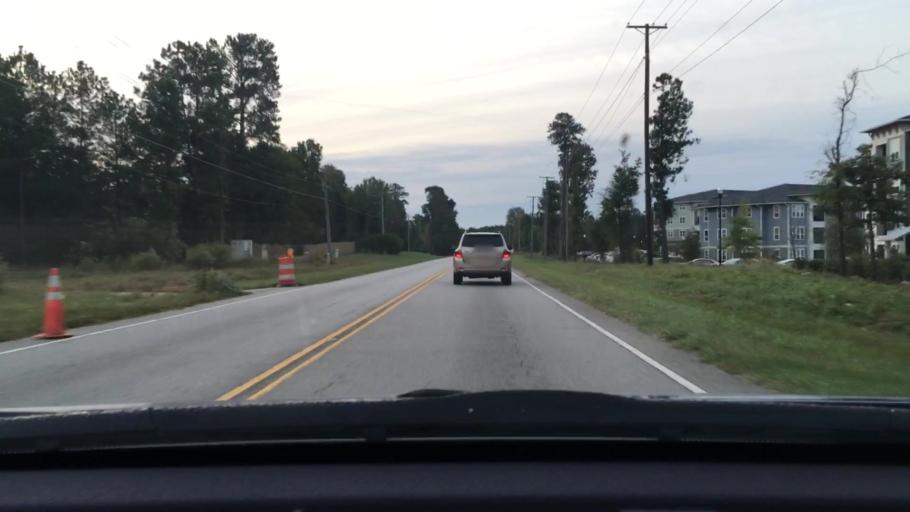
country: US
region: South Carolina
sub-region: Lexington County
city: Irmo
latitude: 34.0920
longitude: -81.1531
